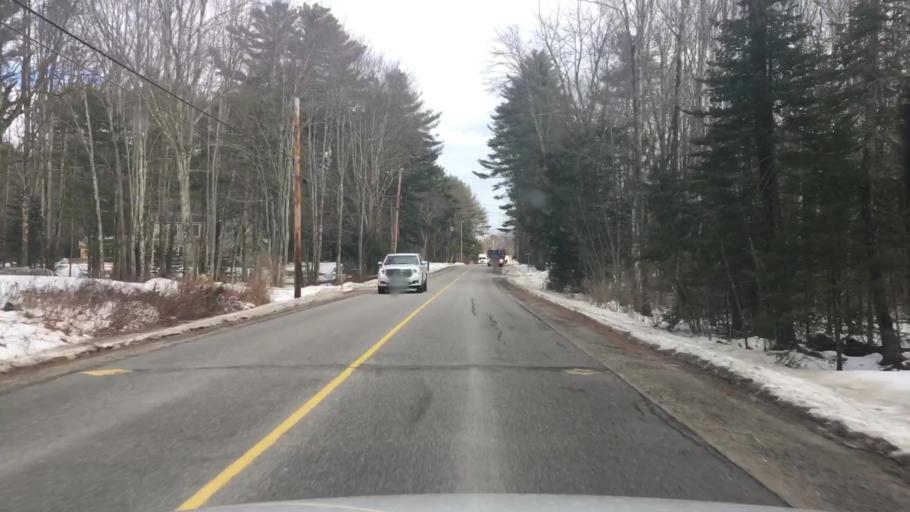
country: US
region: Maine
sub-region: York County
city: Kennebunk
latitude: 43.4052
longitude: -70.5191
